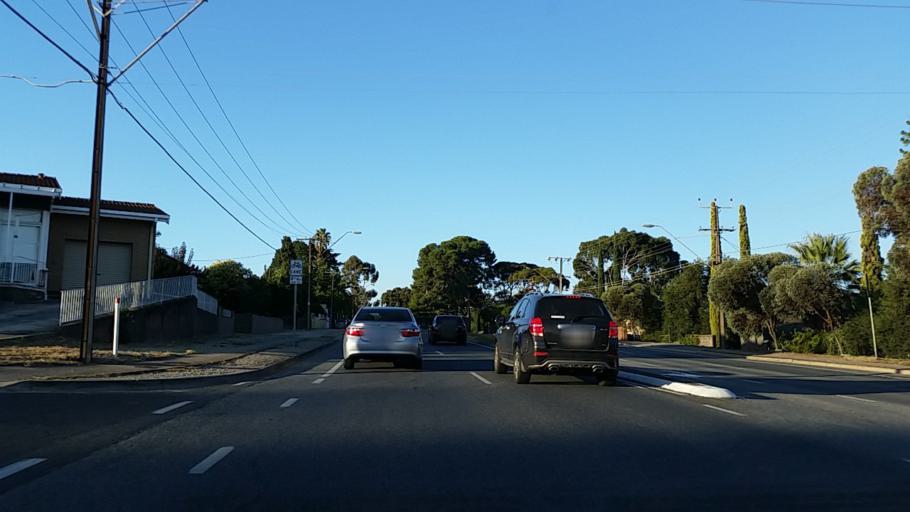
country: AU
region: South Australia
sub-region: Campbelltown
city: Athelstone
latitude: -34.8602
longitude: 138.6850
